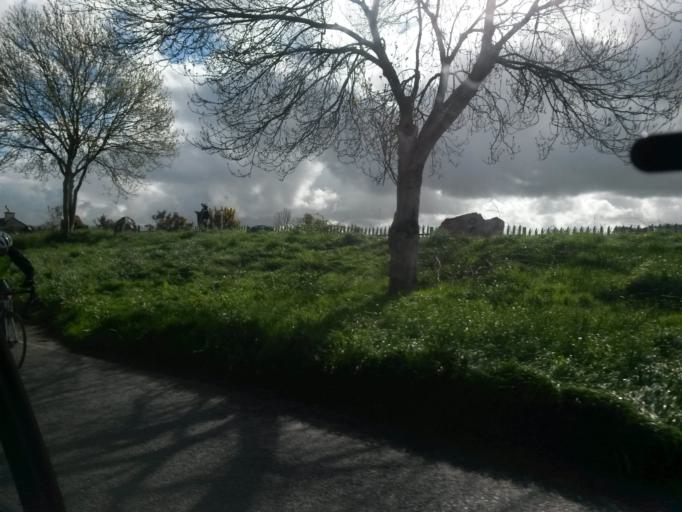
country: IE
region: Leinster
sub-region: Loch Garman
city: Ferns
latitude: 52.5579
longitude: -6.5333
